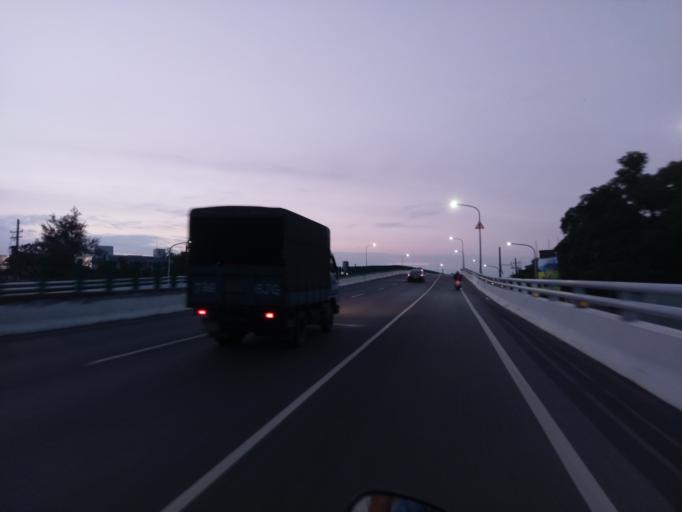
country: TW
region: Taiwan
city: Xinying
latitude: 23.1959
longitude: 120.3207
